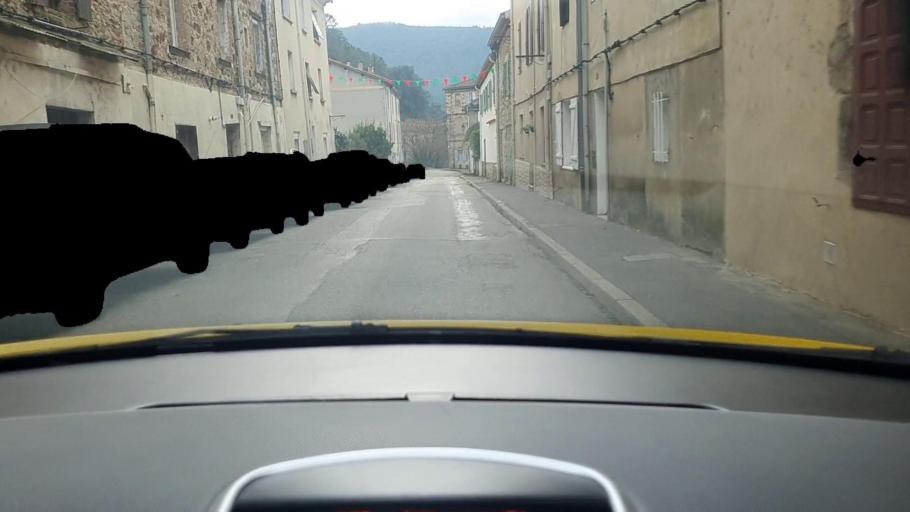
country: FR
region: Languedoc-Roussillon
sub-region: Departement du Gard
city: Besseges
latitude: 44.2990
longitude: 4.0934
